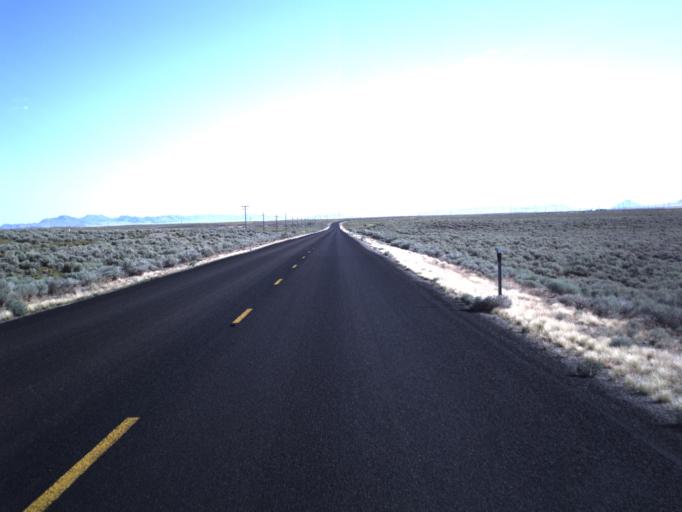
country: US
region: Utah
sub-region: Beaver County
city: Milford
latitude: 38.4457
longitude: -113.0090
